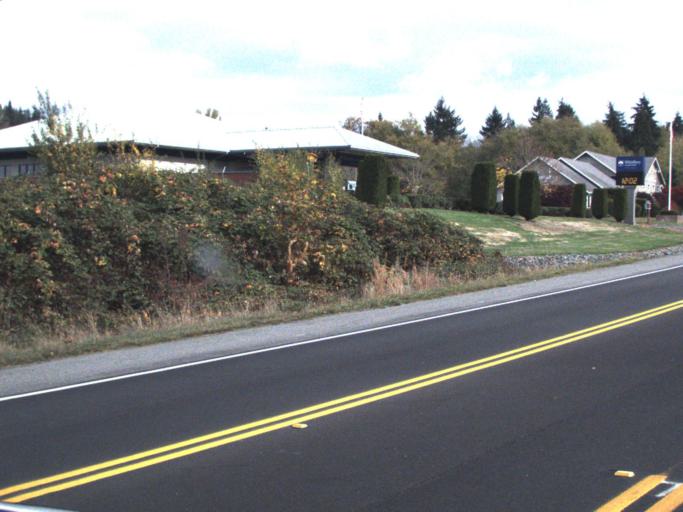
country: US
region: Washington
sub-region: Island County
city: Freeland
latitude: 48.0076
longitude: -122.5252
